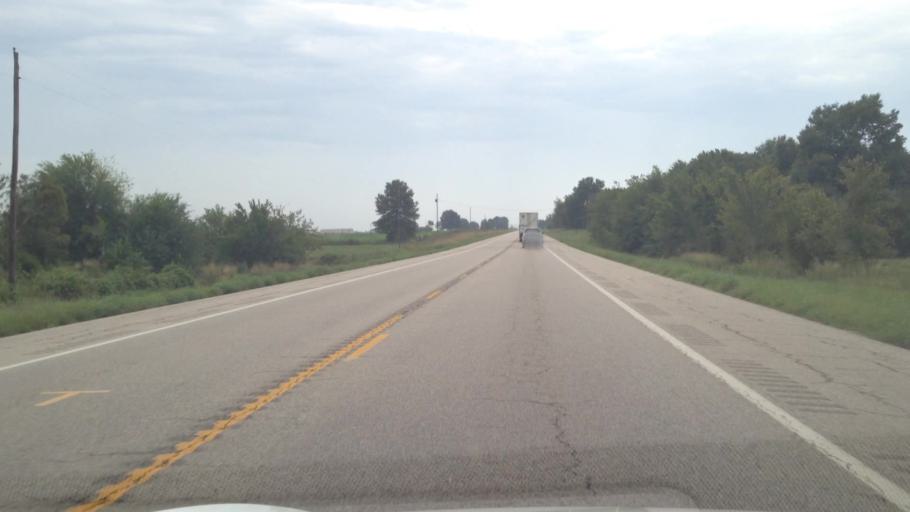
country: US
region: Kansas
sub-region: Crawford County
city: Pittsburg
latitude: 37.2872
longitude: -94.7055
